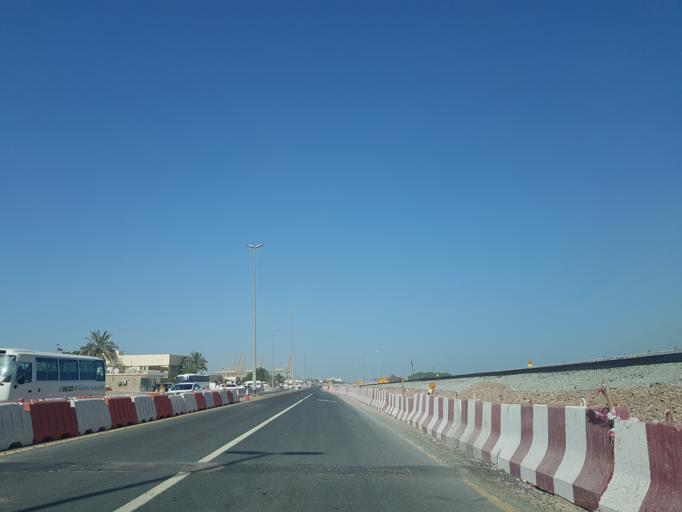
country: AE
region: Dubai
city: Dubai
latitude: 25.0161
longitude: 55.0881
